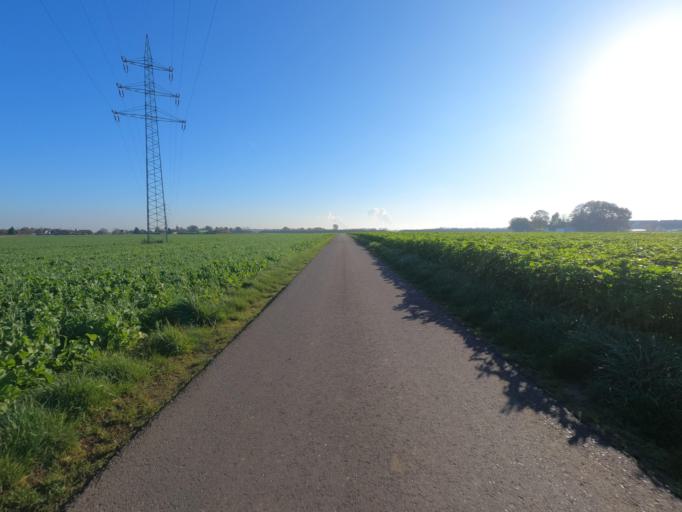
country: DE
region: North Rhine-Westphalia
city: Erkelenz
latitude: 51.0861
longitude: 6.3669
